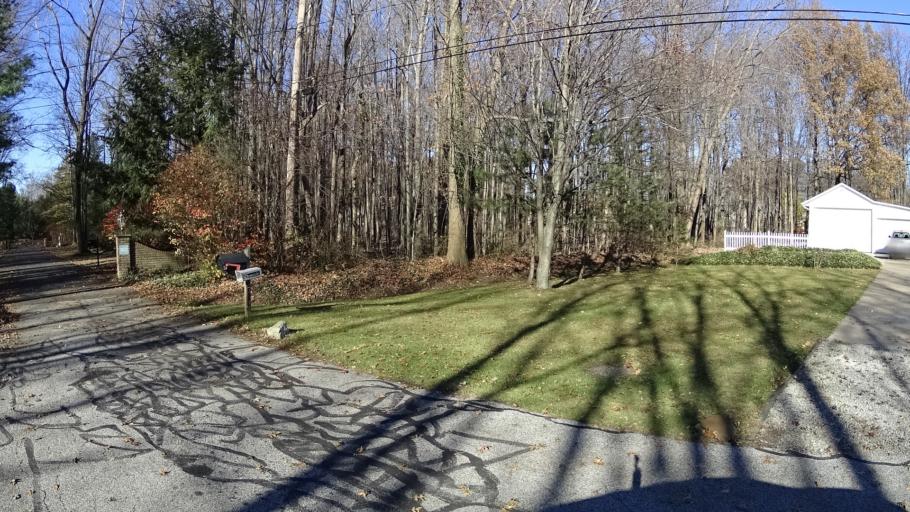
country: US
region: Ohio
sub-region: Lorain County
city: Avon
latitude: 41.4411
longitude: -82.0362
